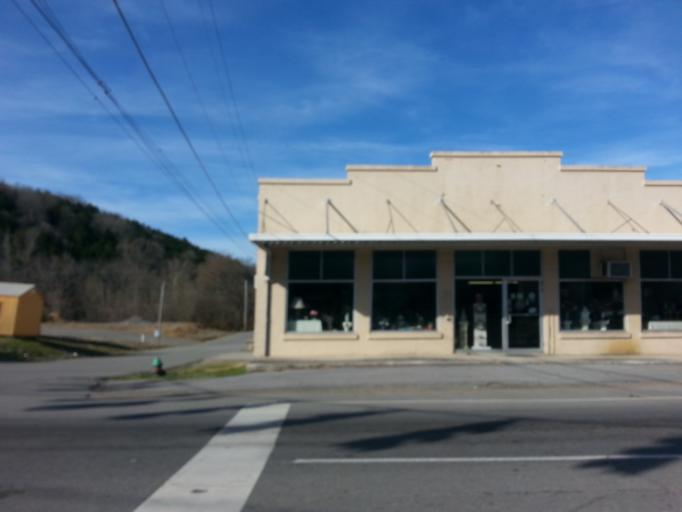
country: US
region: Tennessee
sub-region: Cannon County
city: Woodbury
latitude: 35.8281
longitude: -86.0749
